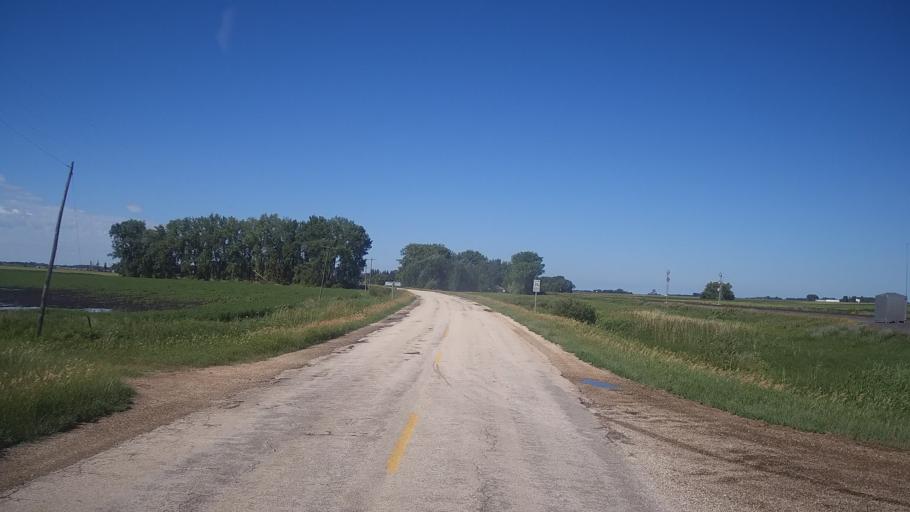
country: CA
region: Manitoba
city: Portage la Prairie
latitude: 50.0411
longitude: -98.0676
